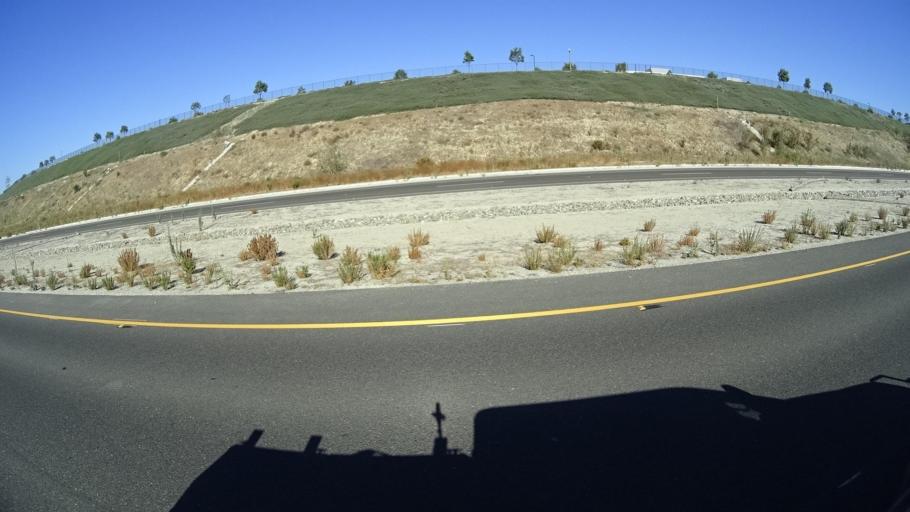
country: US
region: California
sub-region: Orange County
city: Ladera Ranch
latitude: 33.5344
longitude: -117.5947
